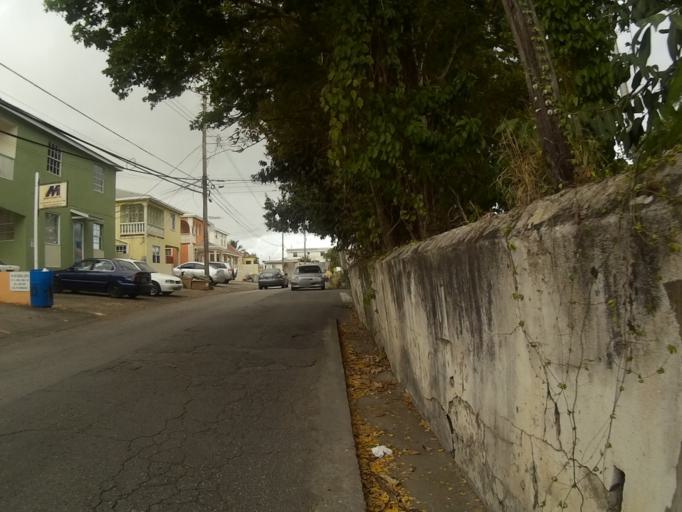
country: BB
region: Saint Michael
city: Bridgetown
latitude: 13.0992
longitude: -59.6034
